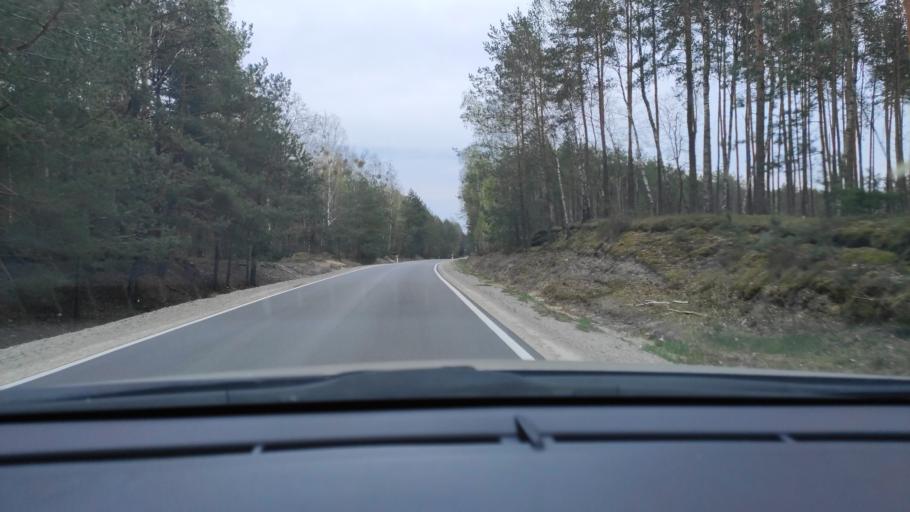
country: PL
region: Masovian Voivodeship
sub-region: Powiat zwolenski
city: Zwolen
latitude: 51.4069
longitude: 21.5257
